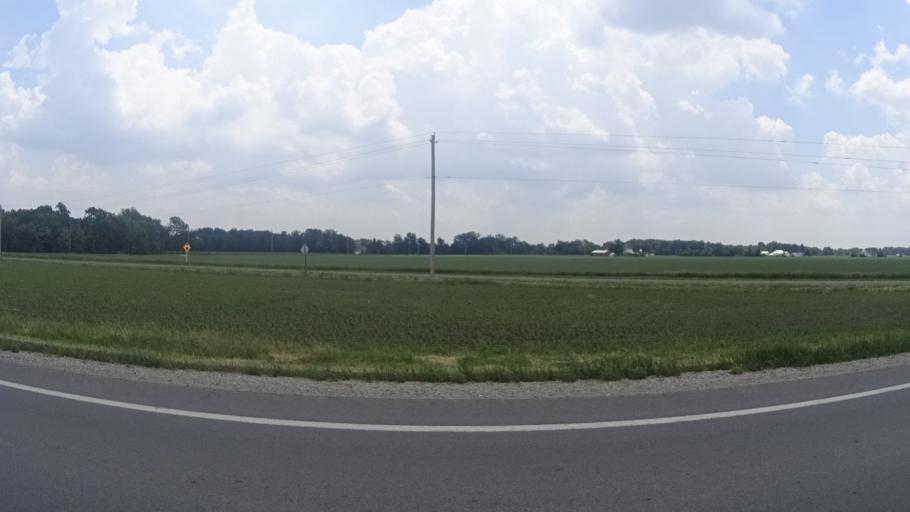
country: US
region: Ohio
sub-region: Huron County
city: Monroeville
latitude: 41.2875
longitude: -82.6791
